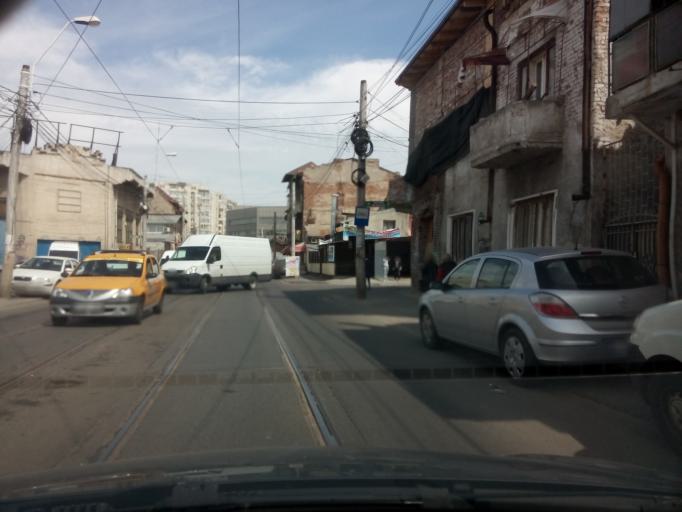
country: RO
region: Bucuresti
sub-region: Municipiul Bucuresti
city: Bucharest
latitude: 44.4540
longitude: 26.1209
